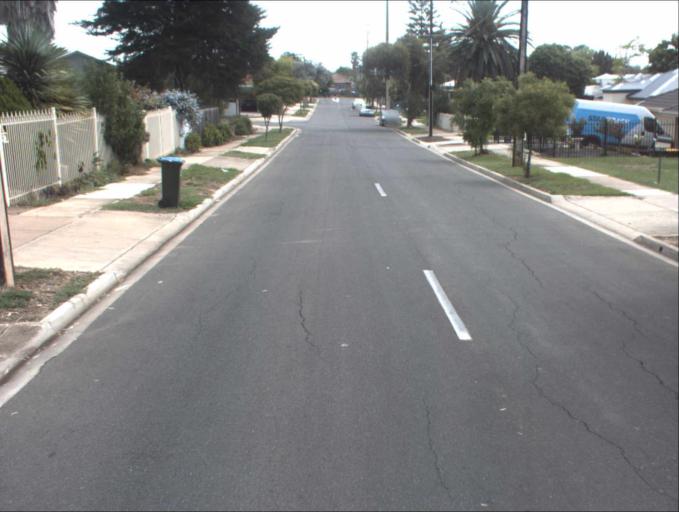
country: AU
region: South Australia
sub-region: Port Adelaide Enfield
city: Enfield
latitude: -34.8607
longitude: 138.6123
